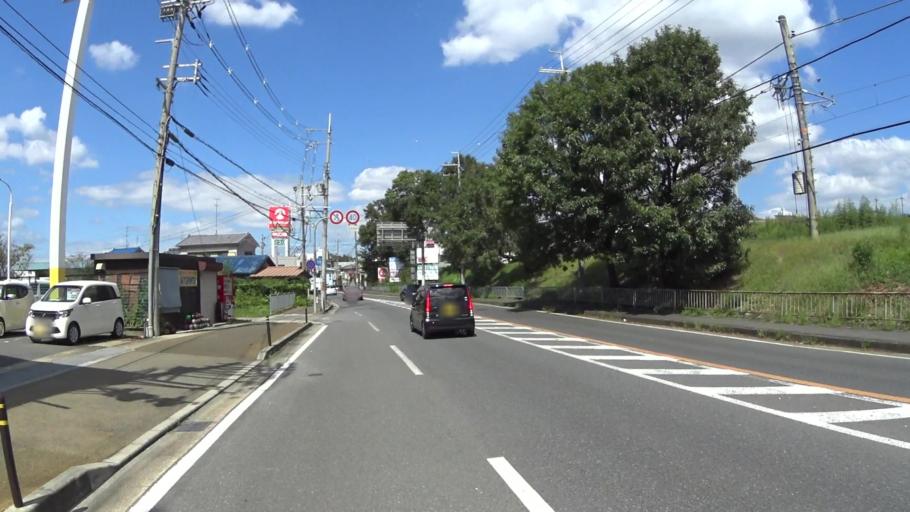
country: JP
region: Kyoto
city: Tanabe
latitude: 34.8475
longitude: 135.7849
